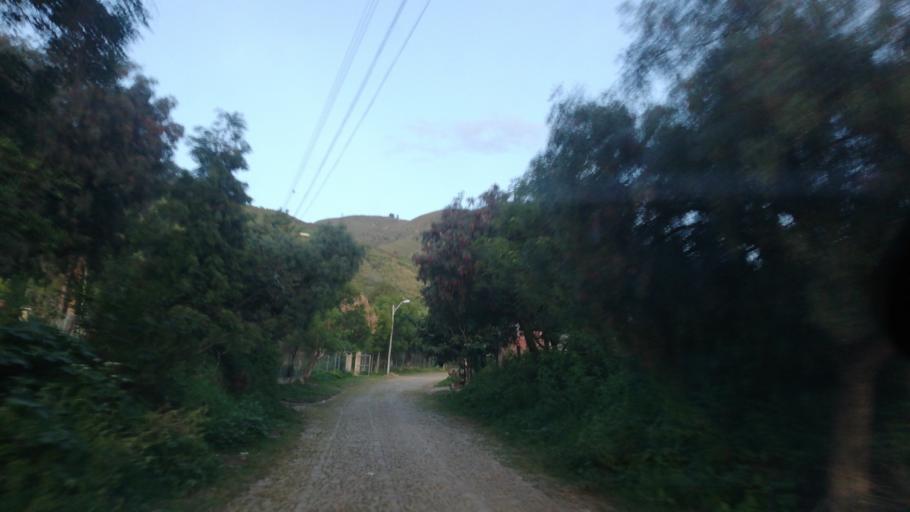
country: BO
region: Cochabamba
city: Cochabamba
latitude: -17.3211
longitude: -66.2085
